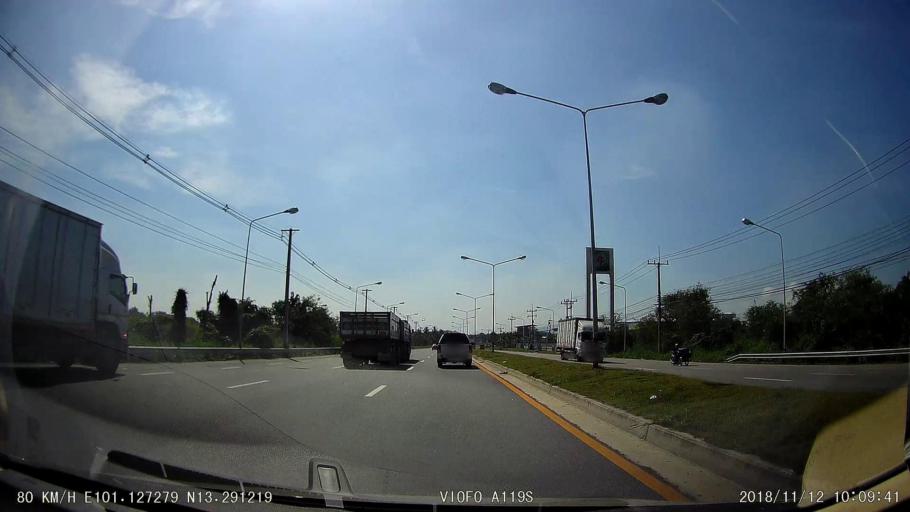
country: TH
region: Chon Buri
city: Ban Bueng
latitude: 13.2911
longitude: 101.1273
